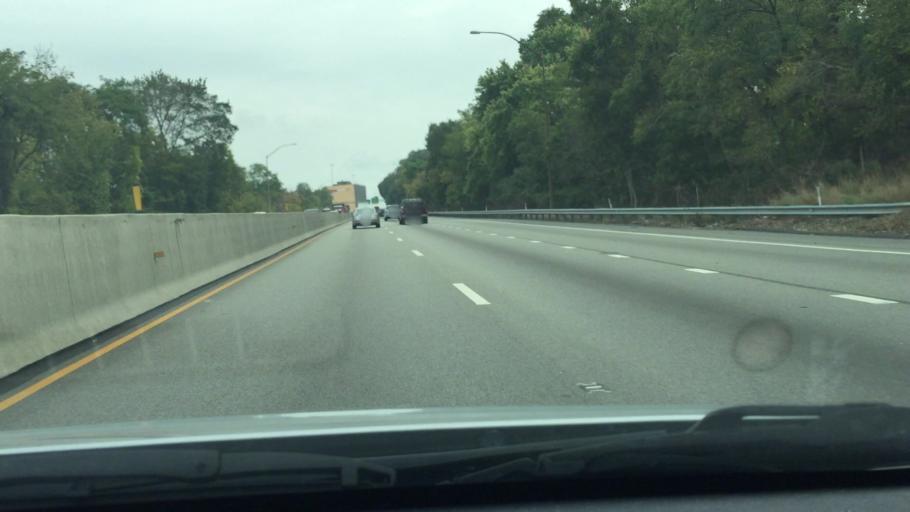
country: US
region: Pennsylvania
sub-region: Allegheny County
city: Green Tree
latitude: 40.4167
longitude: -80.0577
